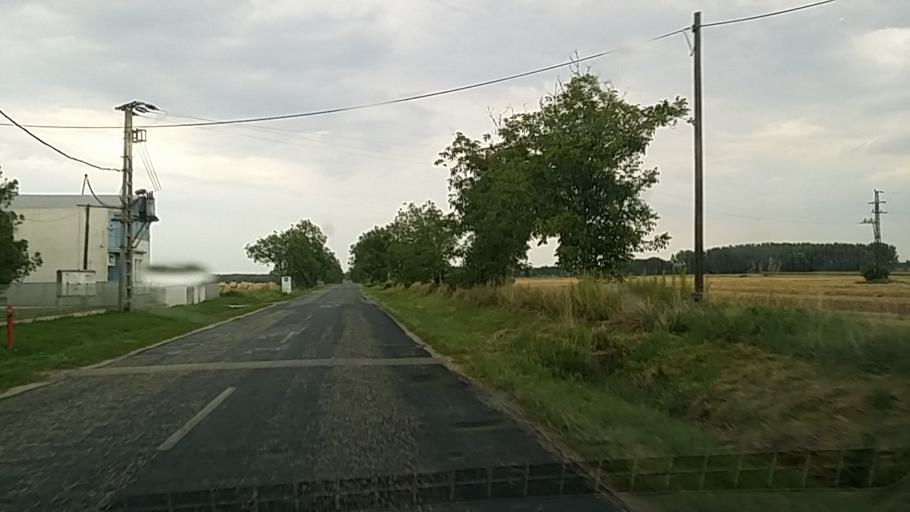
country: HU
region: Zala
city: Zalakomar
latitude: 46.5218
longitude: 17.1333
